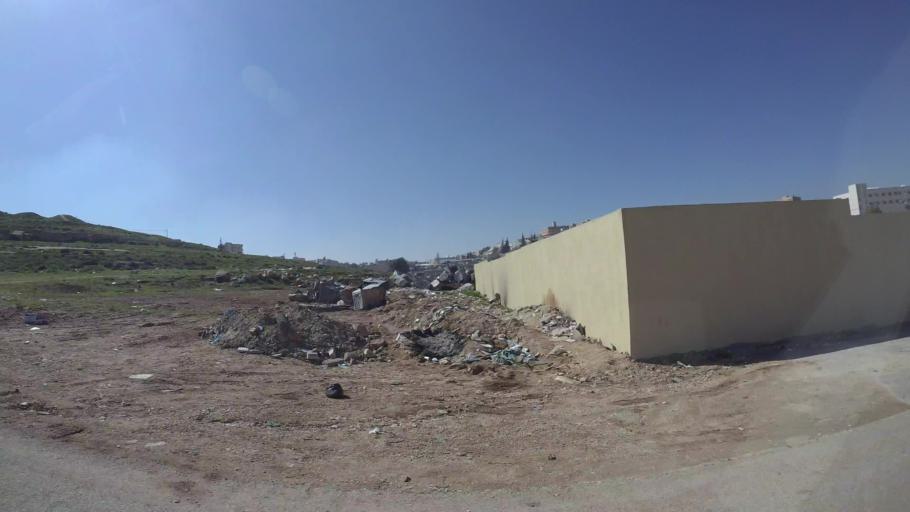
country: JO
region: Amman
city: Al Bunayyat ash Shamaliyah
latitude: 31.9099
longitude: 35.9088
